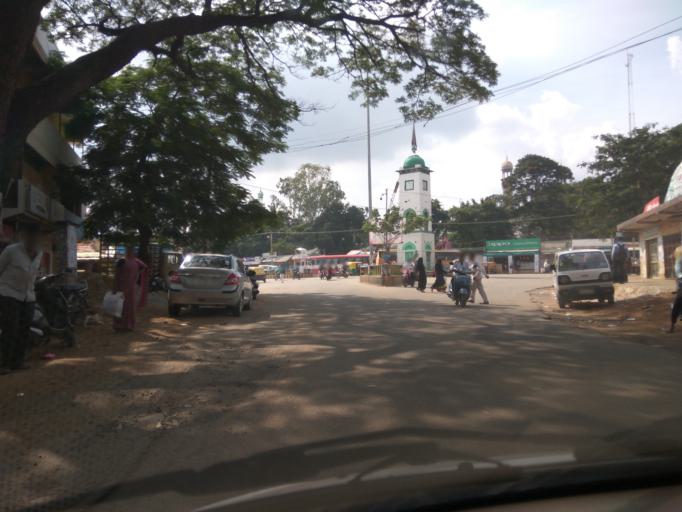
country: IN
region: Karnataka
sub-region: Kolar
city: Kolar
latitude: 13.1319
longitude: 78.1269
